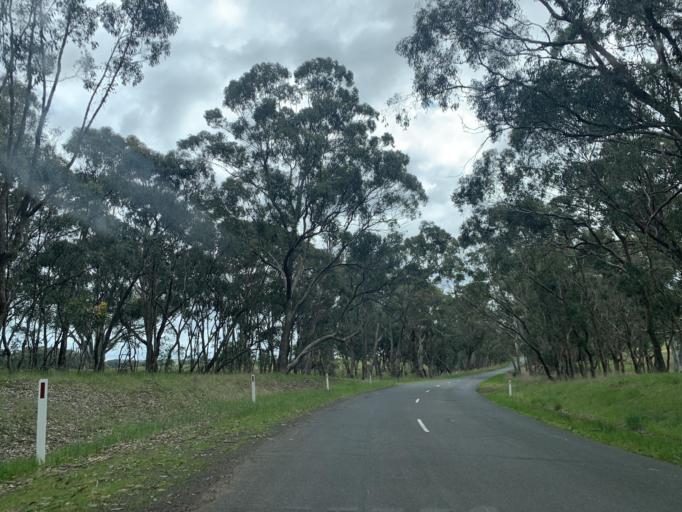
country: AU
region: Victoria
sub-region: Whittlesea
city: Whittlesea
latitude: -37.1400
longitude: 144.9644
